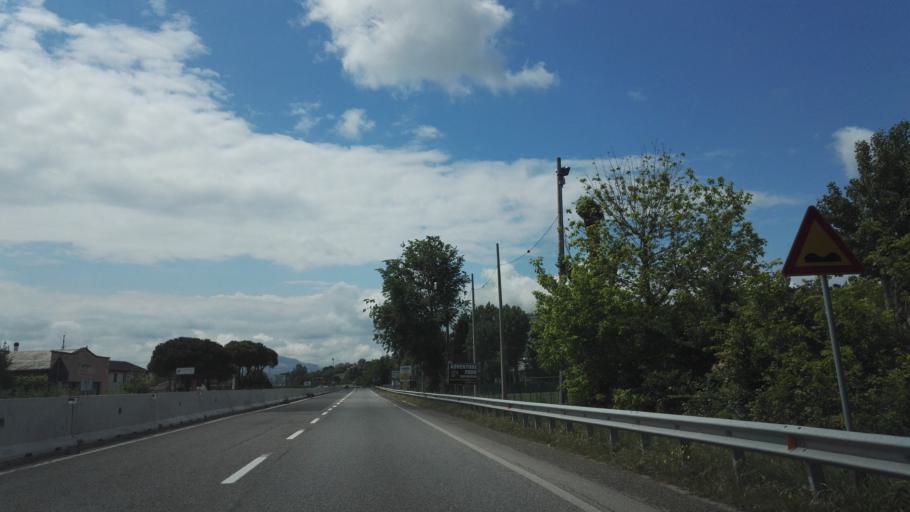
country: IT
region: Emilia-Romagna
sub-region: Provincia di Rimini
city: Rimini
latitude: 44.0340
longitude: 12.5596
